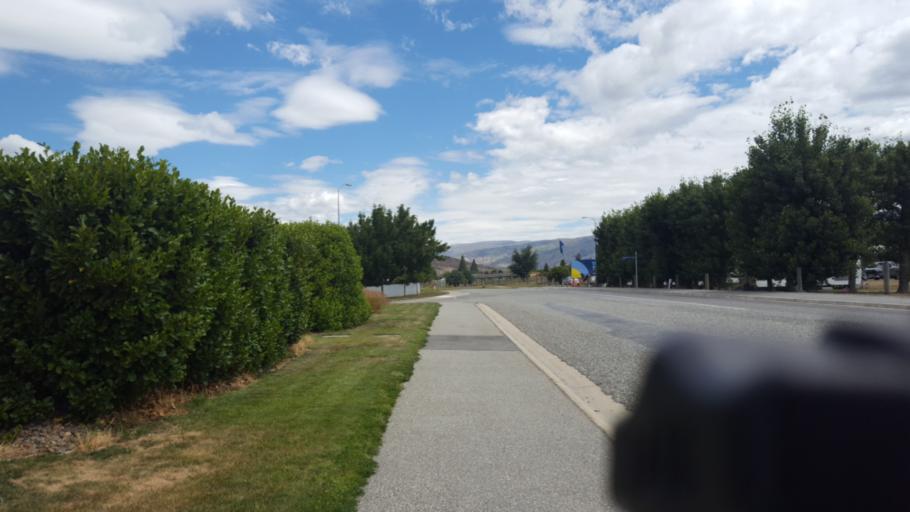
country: NZ
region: Otago
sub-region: Queenstown-Lakes District
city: Wanaka
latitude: -45.0396
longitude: 169.2154
